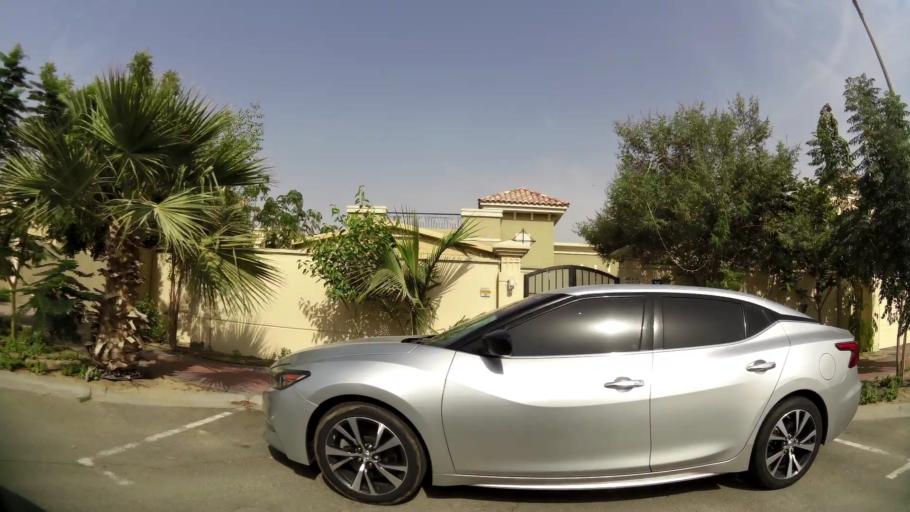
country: AE
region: Ash Shariqah
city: Sharjah
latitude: 25.2705
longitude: 55.4570
